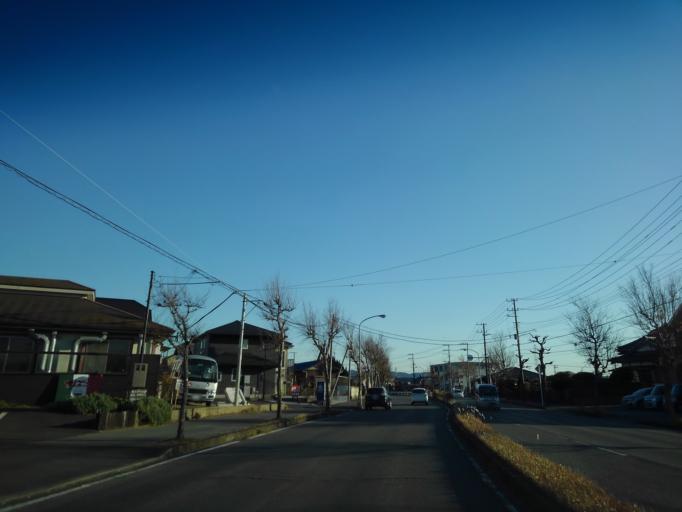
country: JP
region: Chiba
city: Kimitsu
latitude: 35.3234
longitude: 139.9111
